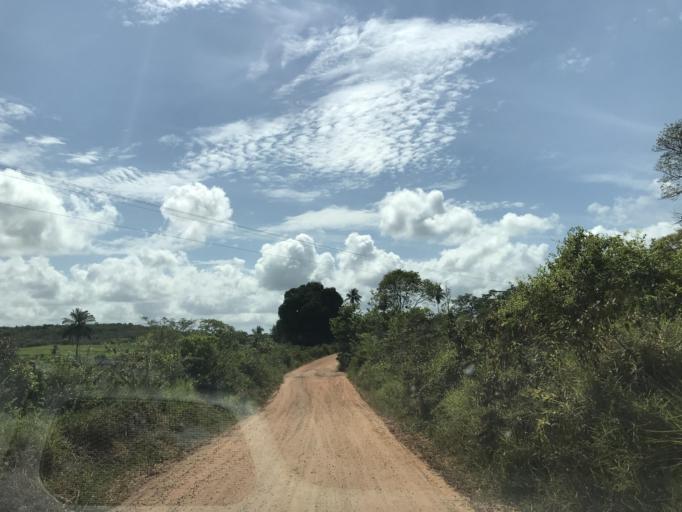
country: BR
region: Bahia
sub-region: Entre Rios
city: Entre Rios
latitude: -12.1800
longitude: -38.0598
